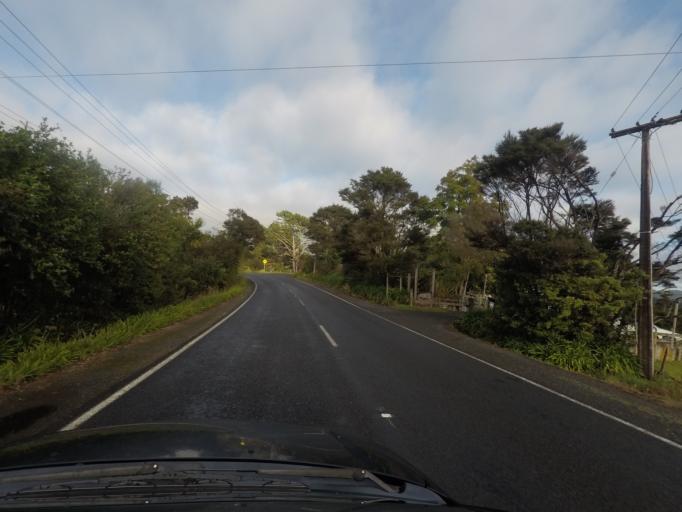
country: NZ
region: Auckland
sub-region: Auckland
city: Waitakere
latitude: -36.9119
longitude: 174.6069
